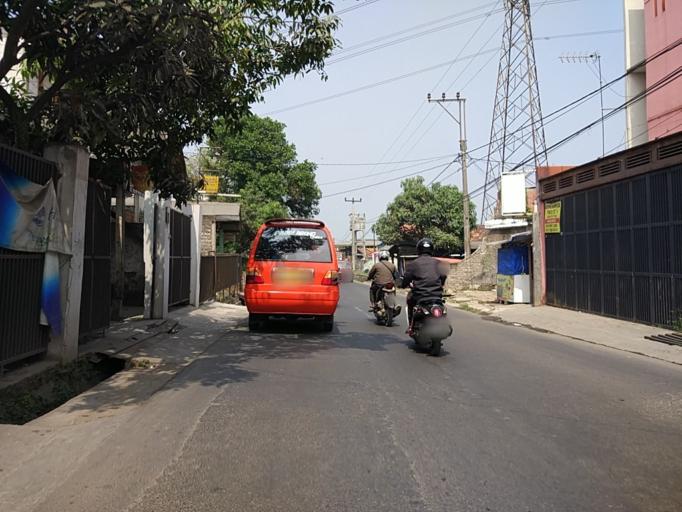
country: ID
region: West Java
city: Padalarang
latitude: -6.8472
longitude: 107.4978
